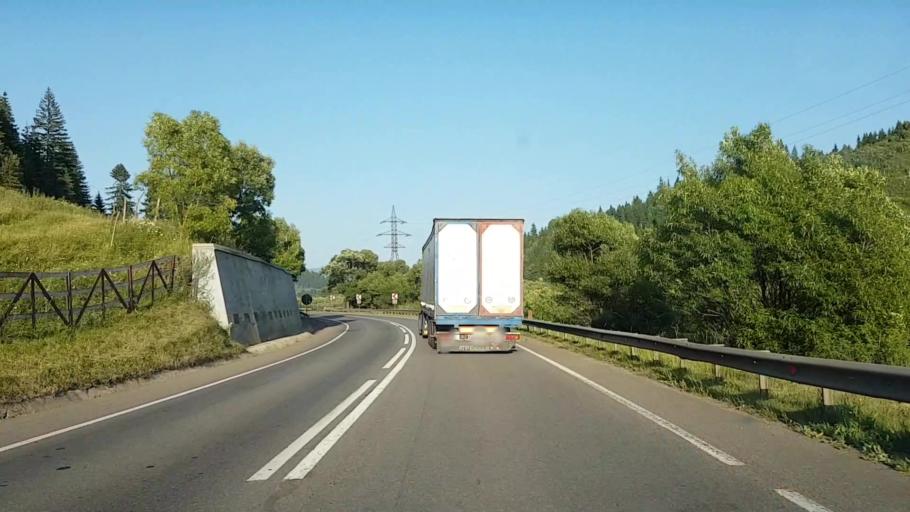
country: RO
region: Suceava
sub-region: Comuna Dorna Candrenilor
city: Dorna Candrenilor
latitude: 47.3556
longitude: 25.2824
